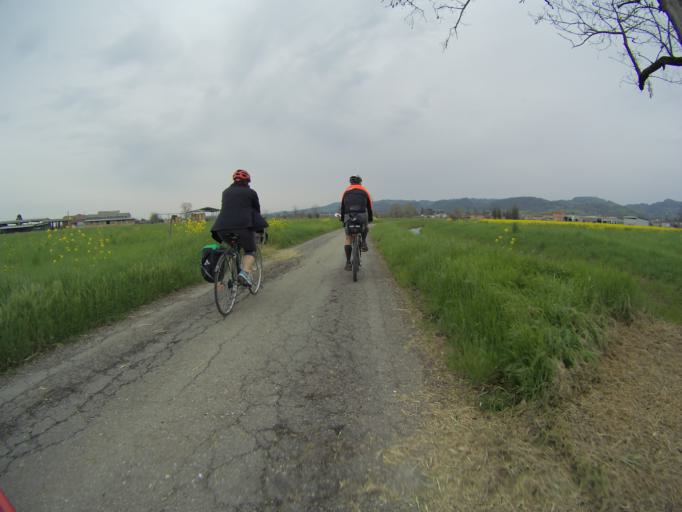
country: IT
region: Emilia-Romagna
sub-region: Provincia di Reggio Emilia
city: San Polo d'Enza
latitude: 44.6494
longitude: 10.4435
